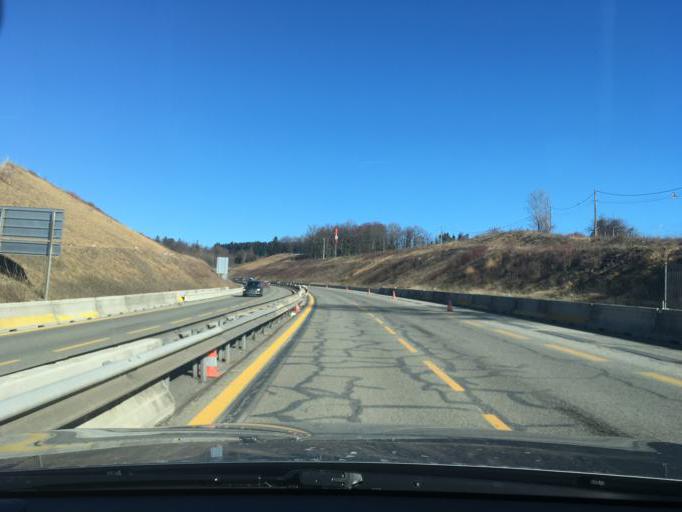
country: FR
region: Rhone-Alpes
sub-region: Departement de la Haute-Savoie
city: Pringy
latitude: 45.9520
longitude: 6.1227
